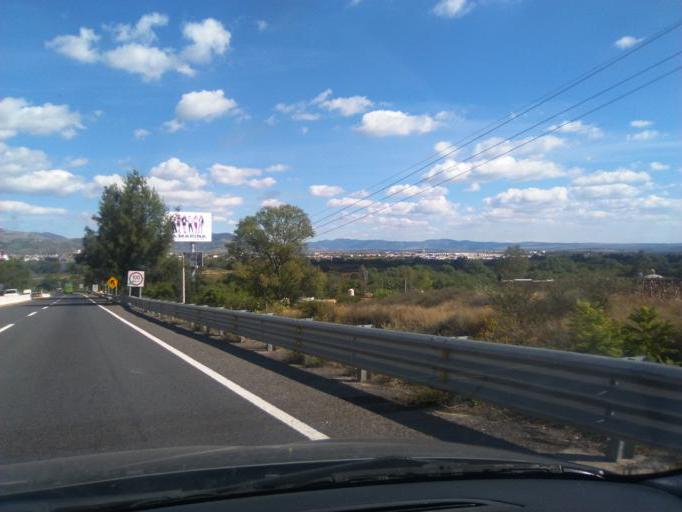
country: MX
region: Guanajuato
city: Santa Teresa
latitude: 20.9685
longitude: -101.3154
